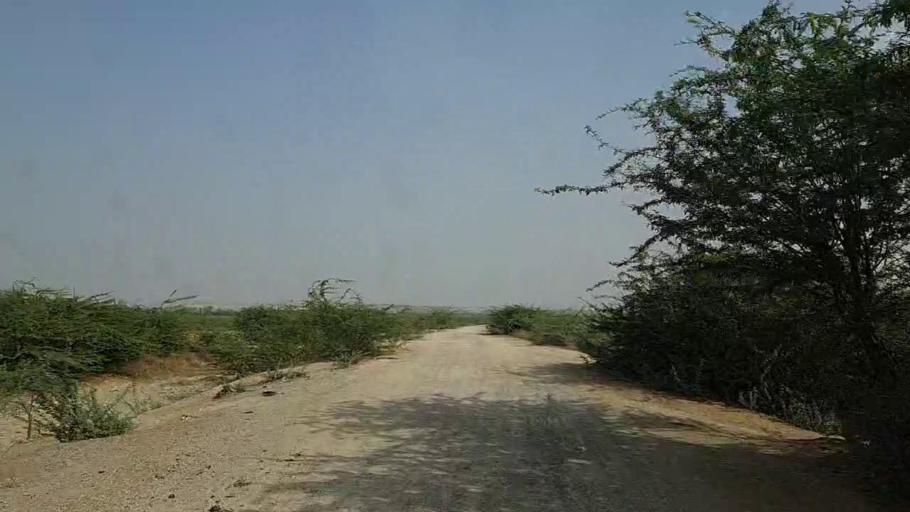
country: PK
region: Sindh
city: Naukot
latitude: 24.6670
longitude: 69.2752
